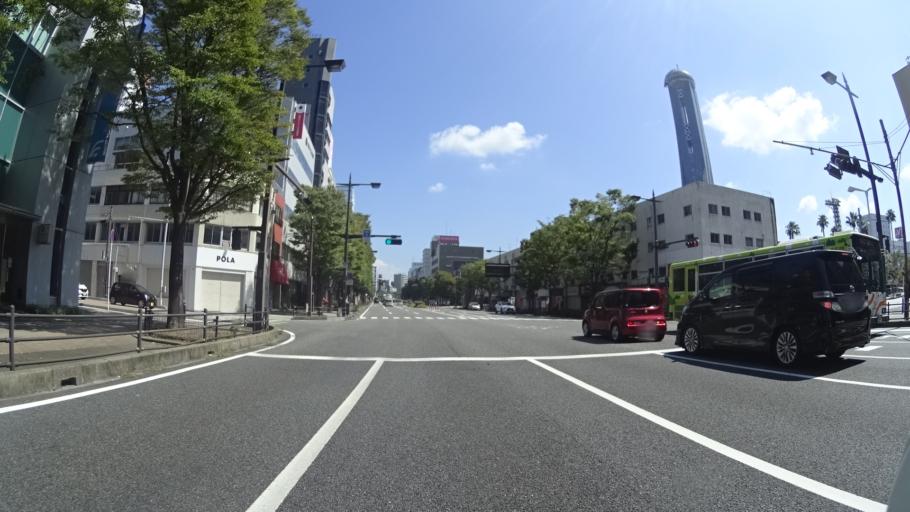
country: JP
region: Yamaguchi
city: Shimonoseki
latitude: 33.9508
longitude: 130.9270
